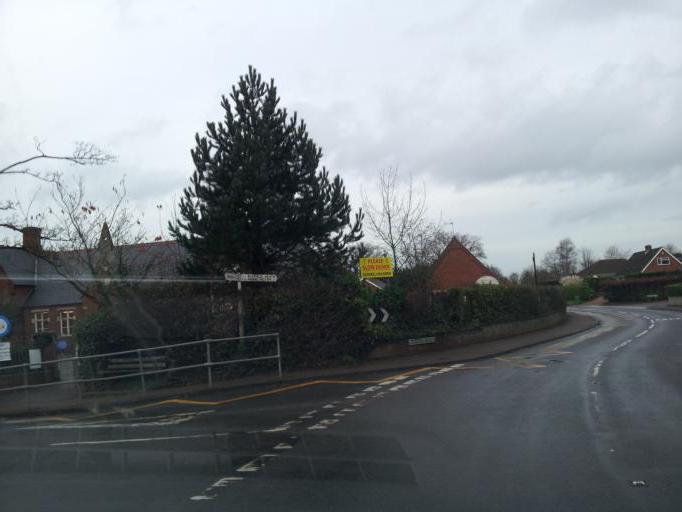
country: GB
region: England
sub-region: Norfolk
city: Brundall
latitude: 52.6365
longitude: 1.4485
